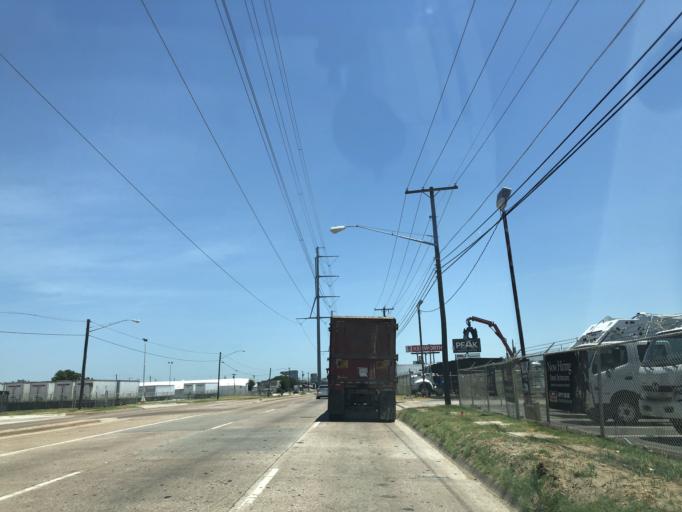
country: US
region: Texas
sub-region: Dallas County
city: Irving
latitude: 32.8080
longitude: -96.8885
